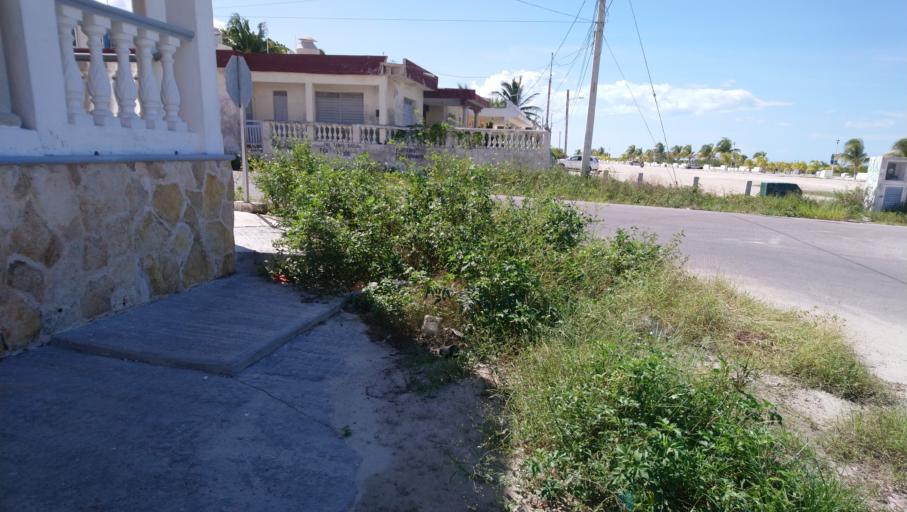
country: MX
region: Yucatan
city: Progreso de Castro
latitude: 21.2844
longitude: -89.6709
